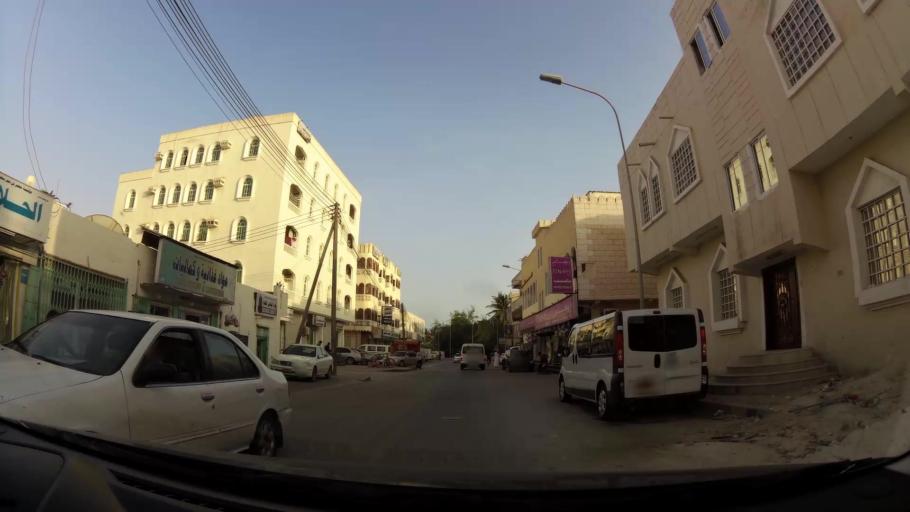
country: OM
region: Zufar
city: Salalah
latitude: 17.0135
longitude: 54.1031
